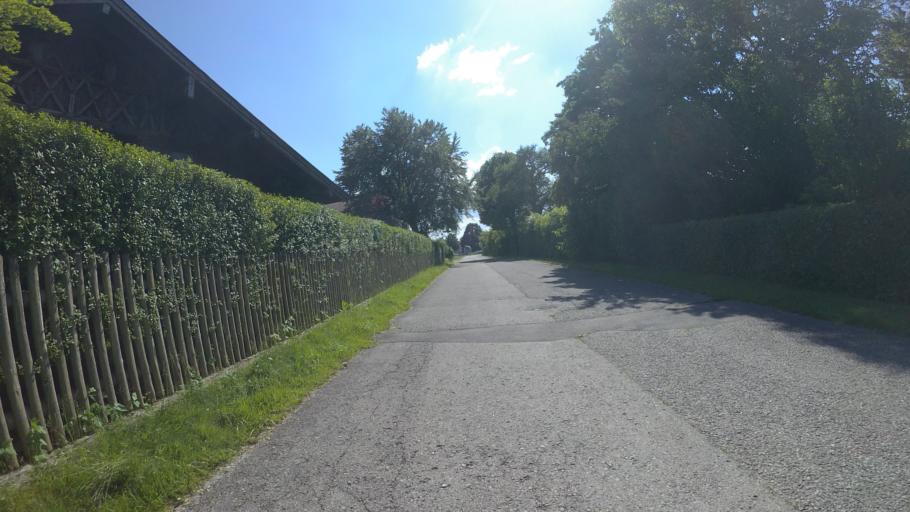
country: DE
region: Bavaria
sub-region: Upper Bavaria
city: Seeon-Seebruck
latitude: 47.9621
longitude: 12.5025
